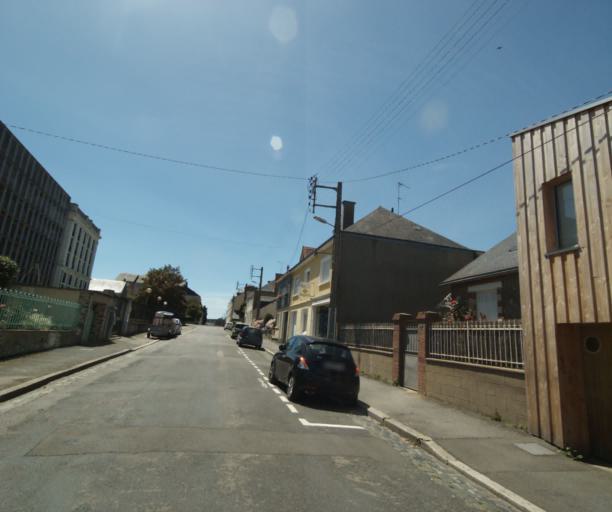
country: FR
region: Pays de la Loire
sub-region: Departement de la Mayenne
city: Laval
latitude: 48.0737
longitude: -0.7590
